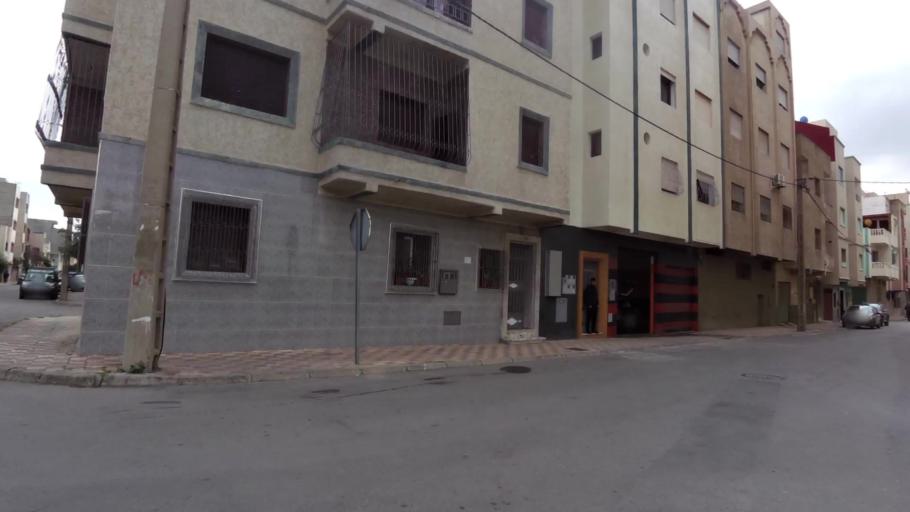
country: MA
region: Tanger-Tetouan
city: Tetouan
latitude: 35.5650
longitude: -5.3620
